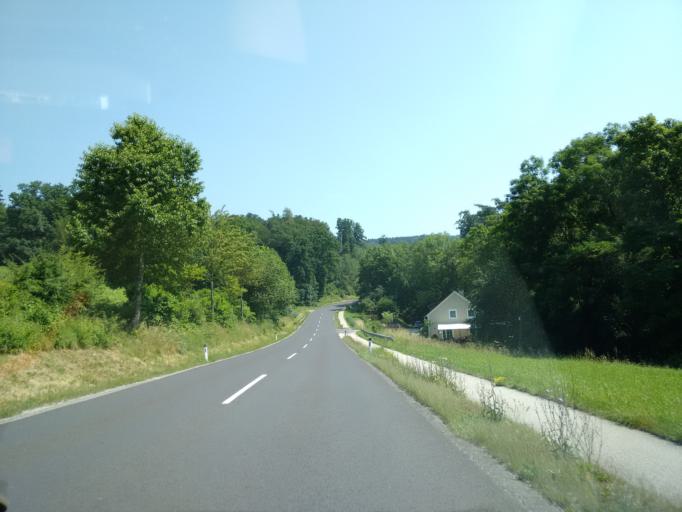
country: AT
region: Upper Austria
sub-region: Politischer Bezirk Urfahr-Umgebung
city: Altenberg bei Linz
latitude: 48.3409
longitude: 14.3289
